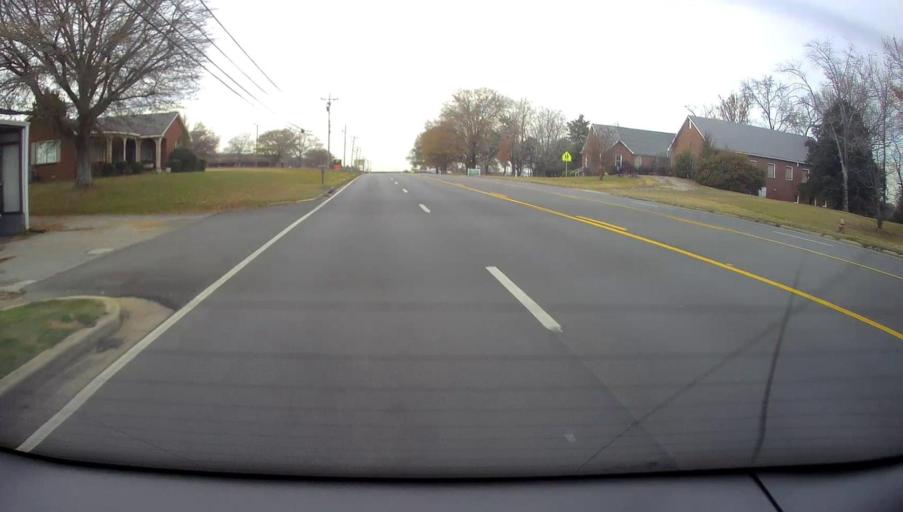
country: US
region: Alabama
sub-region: Morgan County
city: Priceville
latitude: 34.5266
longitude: -86.8968
